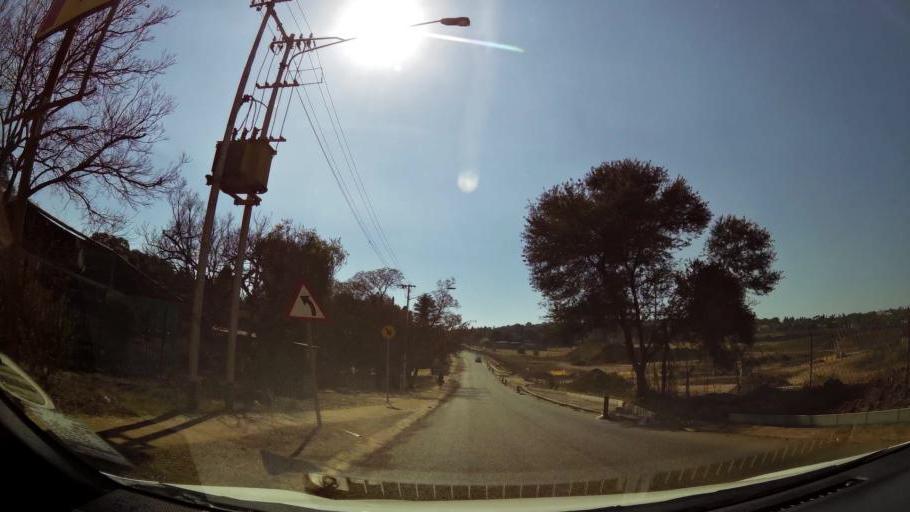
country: ZA
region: Gauteng
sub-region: City of Tshwane Metropolitan Municipality
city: Centurion
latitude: -25.8067
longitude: 28.2334
